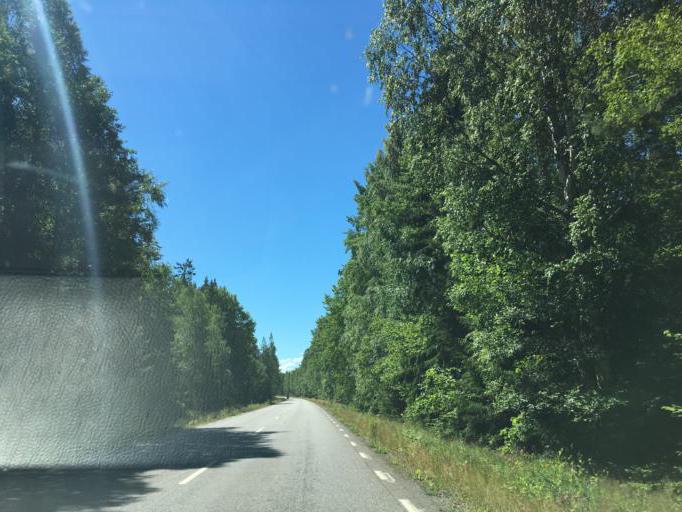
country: SE
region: OErebro
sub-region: Laxa Kommun
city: Laxa
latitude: 58.8071
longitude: 14.5445
